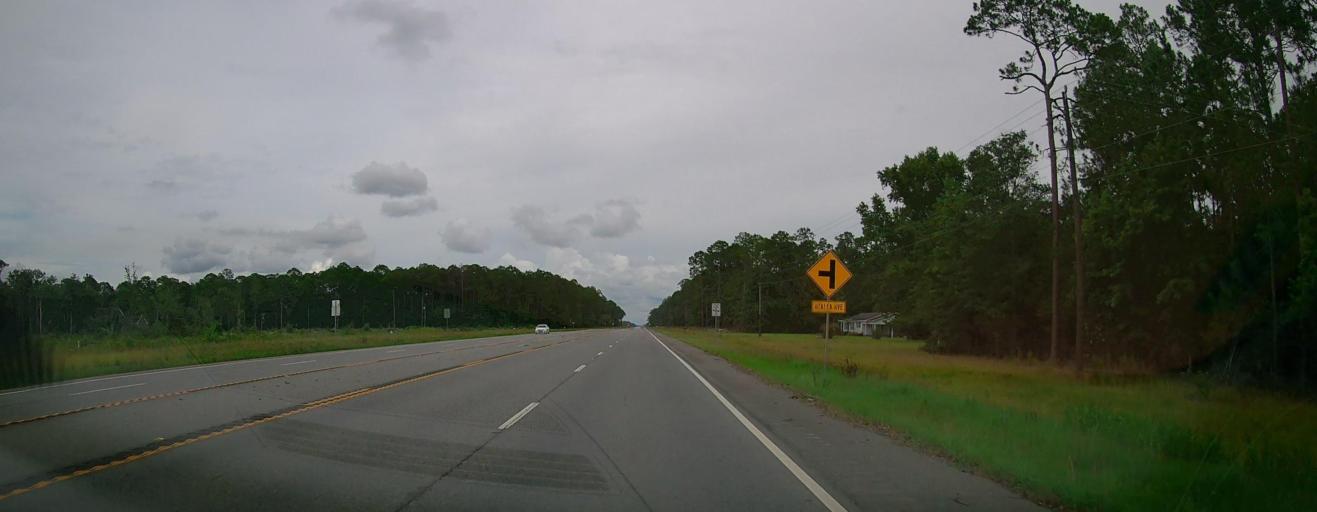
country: US
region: Georgia
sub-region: Appling County
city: Baxley
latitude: 31.7655
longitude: -82.3112
